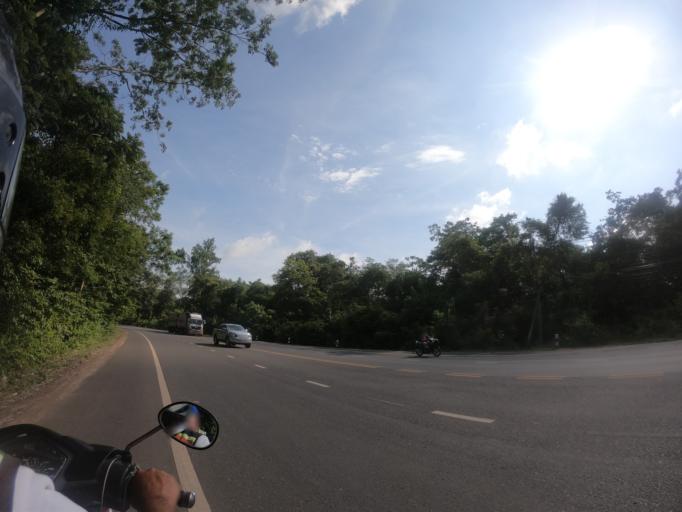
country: TH
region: Surin
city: Kap Choeng
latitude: 14.4482
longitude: 103.7006
